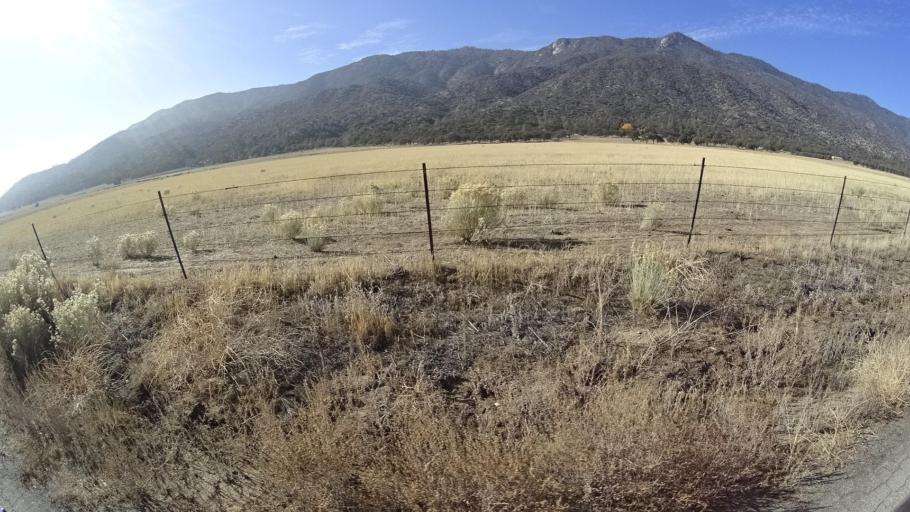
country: US
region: California
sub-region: Kern County
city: Bodfish
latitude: 35.4190
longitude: -118.5365
